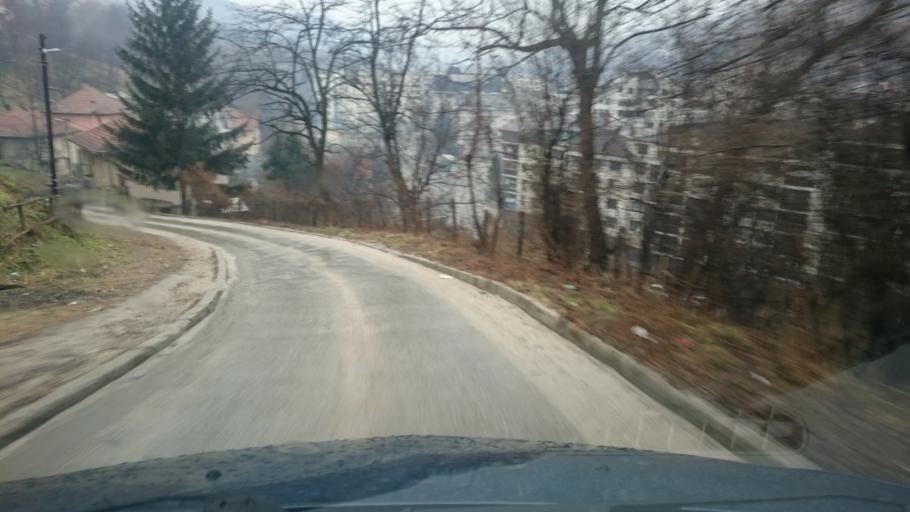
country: BA
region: Federation of Bosnia and Herzegovina
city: Travnik
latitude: 44.2242
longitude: 17.6701
